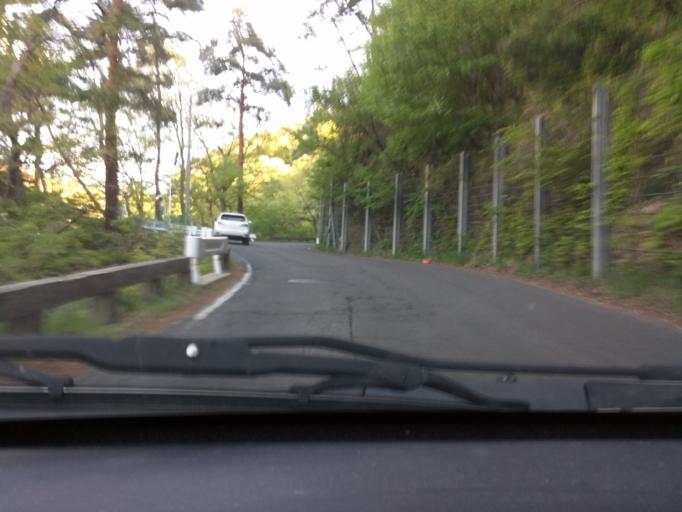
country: JP
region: Nagano
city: Nagano-shi
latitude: 36.6743
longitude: 138.1737
